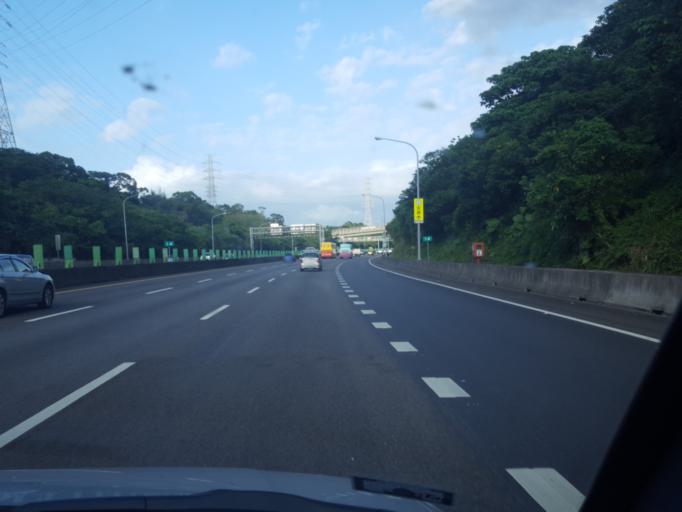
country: TW
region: Taipei
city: Taipei
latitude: 25.0507
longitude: 121.6284
